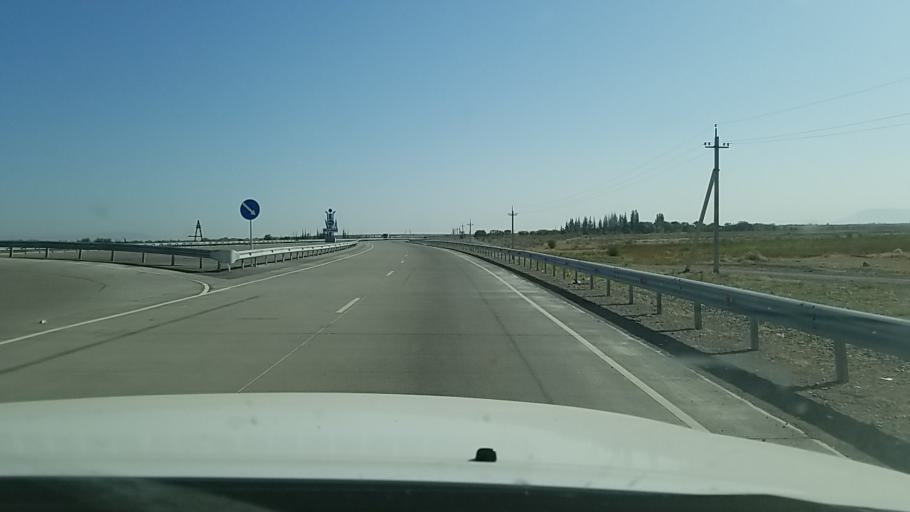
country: KZ
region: Almaty Oblysy
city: Turgen'
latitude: 43.5974
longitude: 78.2896
